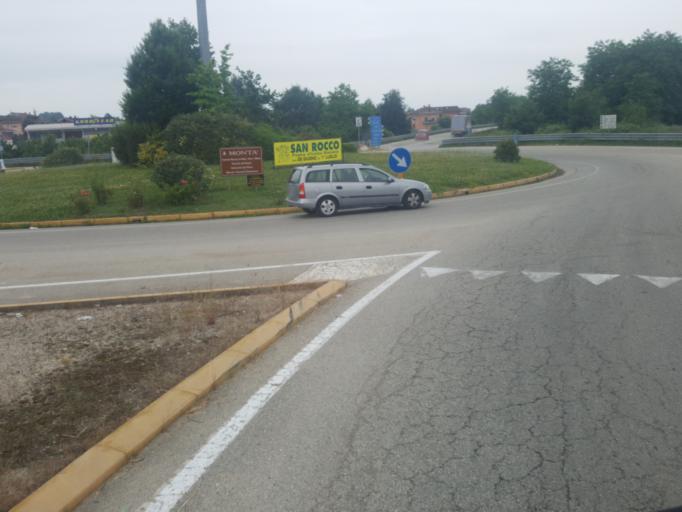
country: IT
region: Piedmont
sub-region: Provincia di Cuneo
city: Monta
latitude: 44.8216
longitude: 7.9475
